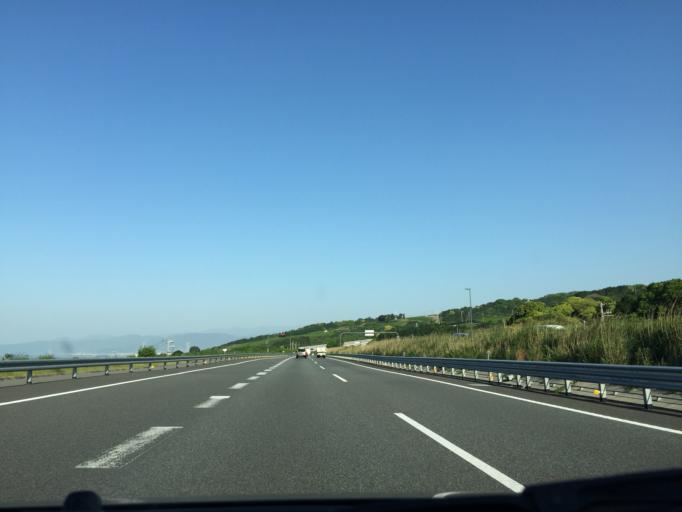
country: JP
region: Shizuoka
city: Numazu
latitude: 35.1536
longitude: 138.8037
